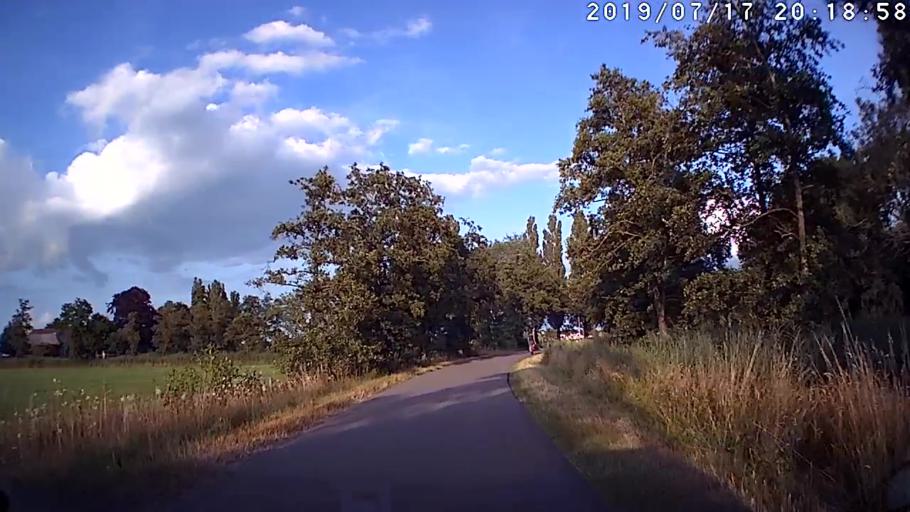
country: NL
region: Overijssel
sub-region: Gemeente Zwolle
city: Zwolle
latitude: 52.5420
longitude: 6.0959
